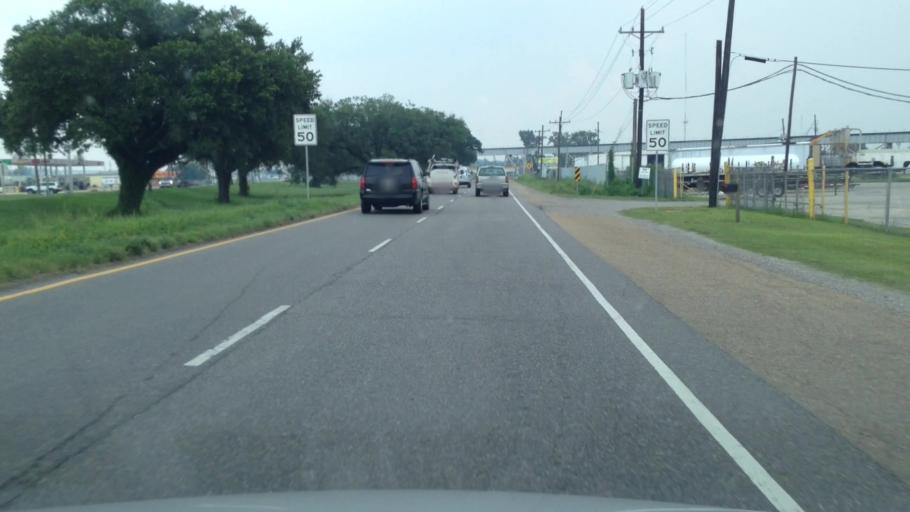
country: US
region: Louisiana
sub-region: West Baton Rouge Parish
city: Port Allen
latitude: 30.5055
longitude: -91.2211
